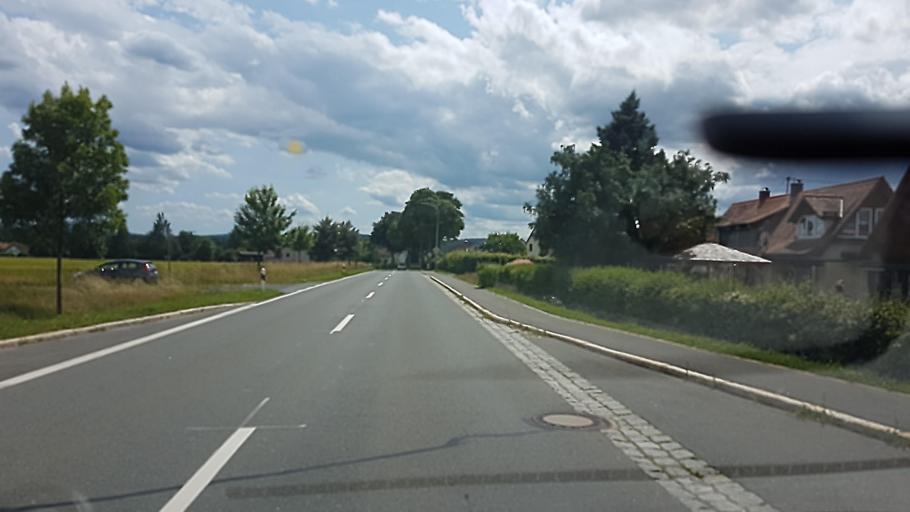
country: DE
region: Bavaria
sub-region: Upper Palatinate
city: Brand
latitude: 49.9656
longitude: 11.9067
